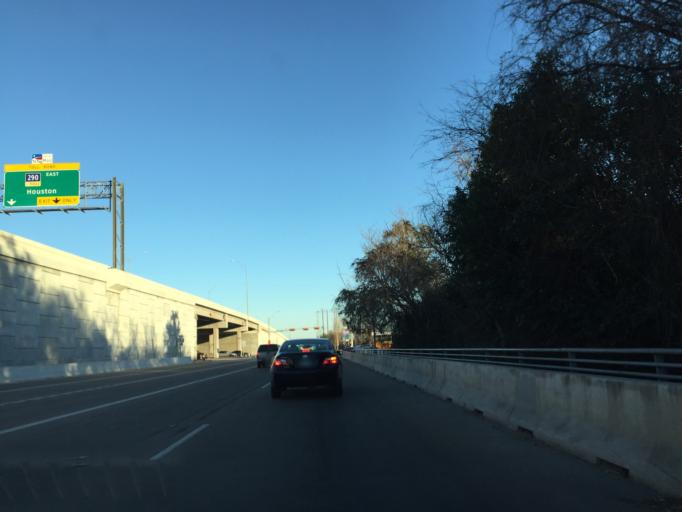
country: US
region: Texas
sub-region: Travis County
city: Austin
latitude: 30.3327
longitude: -97.6880
